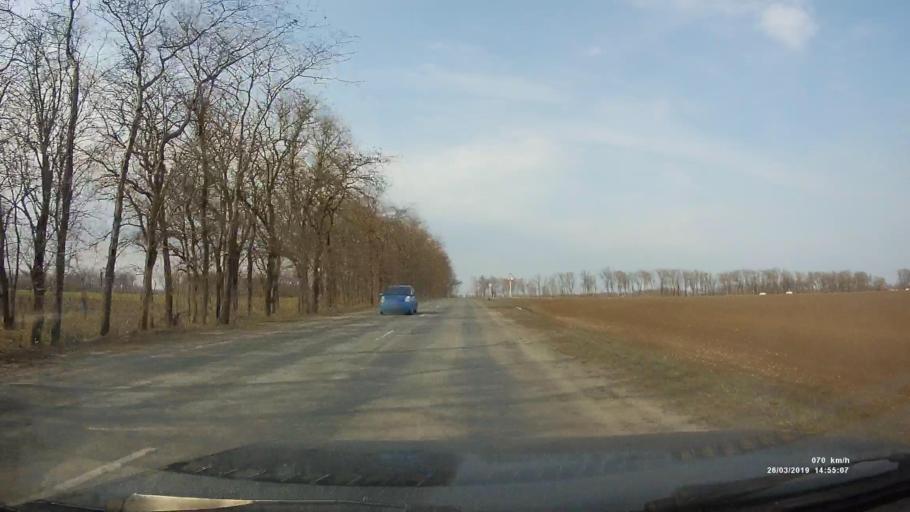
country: RU
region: Rostov
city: Novobessergenovka
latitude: 47.2013
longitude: 38.8107
